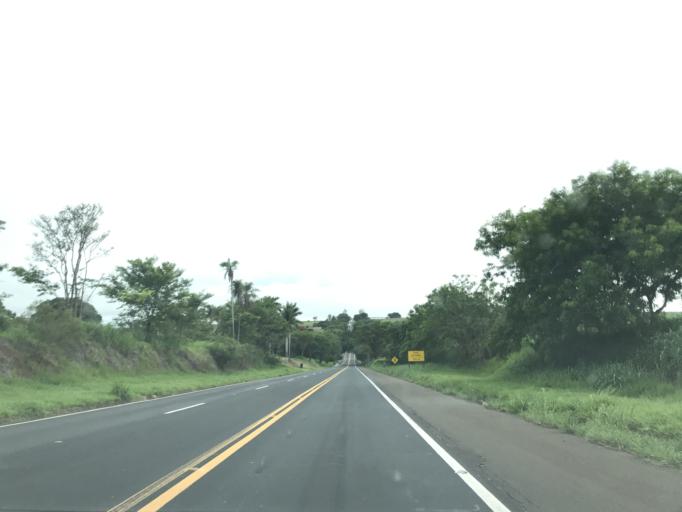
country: BR
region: Sao Paulo
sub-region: Penapolis
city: Penapolis
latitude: -21.4610
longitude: -50.1748
